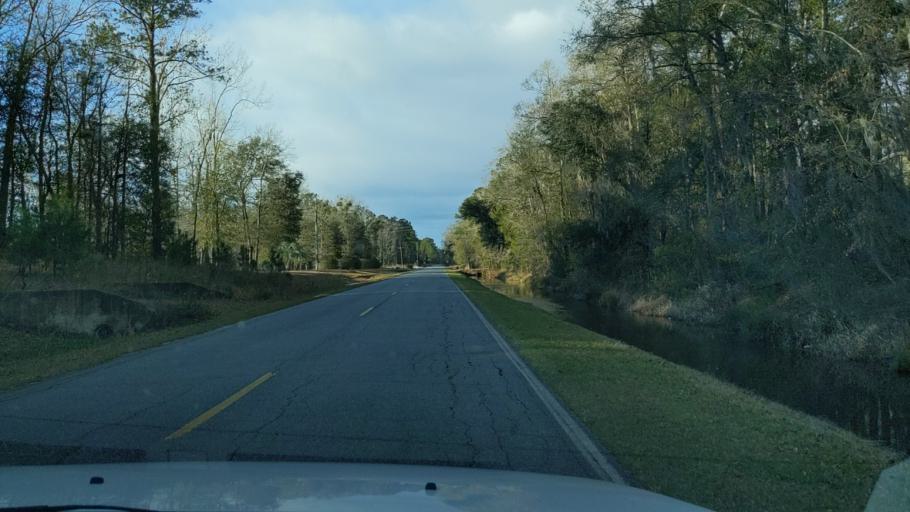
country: US
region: Georgia
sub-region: Chatham County
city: Georgetown
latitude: 32.0399
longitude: -81.2988
